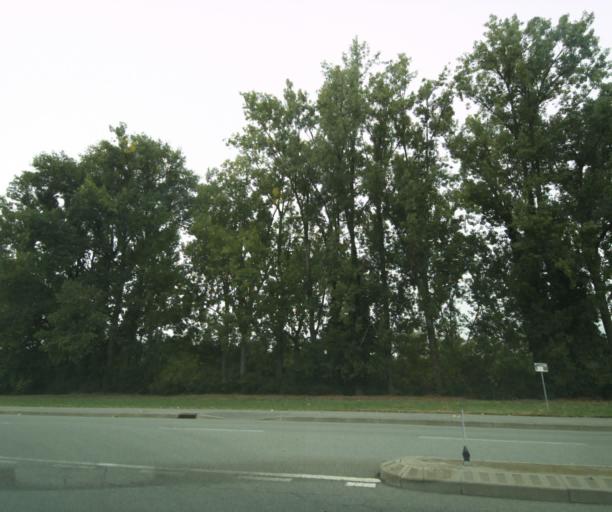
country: FR
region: Auvergne
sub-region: Departement du Puy-de-Dome
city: Gerzat
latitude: 45.8283
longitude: 3.1419
